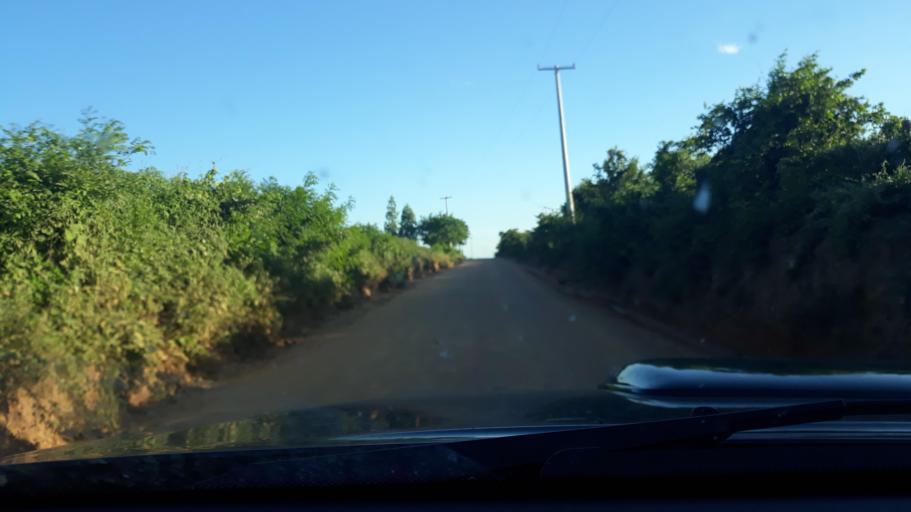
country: BR
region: Bahia
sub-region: Riacho De Santana
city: Riacho de Santana
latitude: -13.7922
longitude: -42.7121
